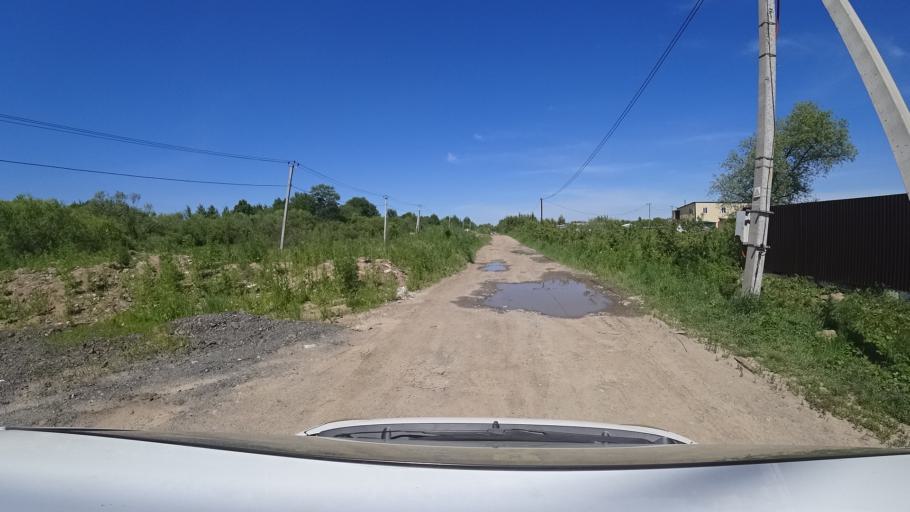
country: RU
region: Khabarovsk Krai
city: Topolevo
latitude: 48.4841
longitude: 135.1756
